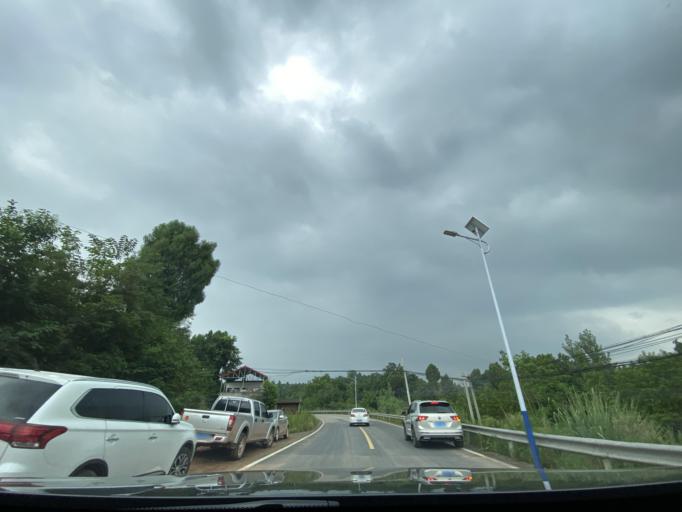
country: CN
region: Sichuan
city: Jiancheng
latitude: 30.5485
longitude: 104.5232
